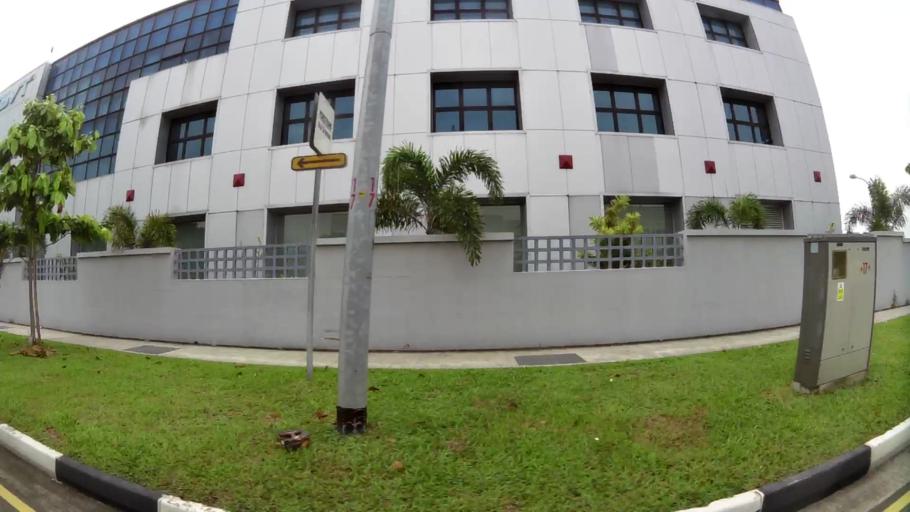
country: SG
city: Singapore
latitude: 1.3532
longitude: 103.9669
